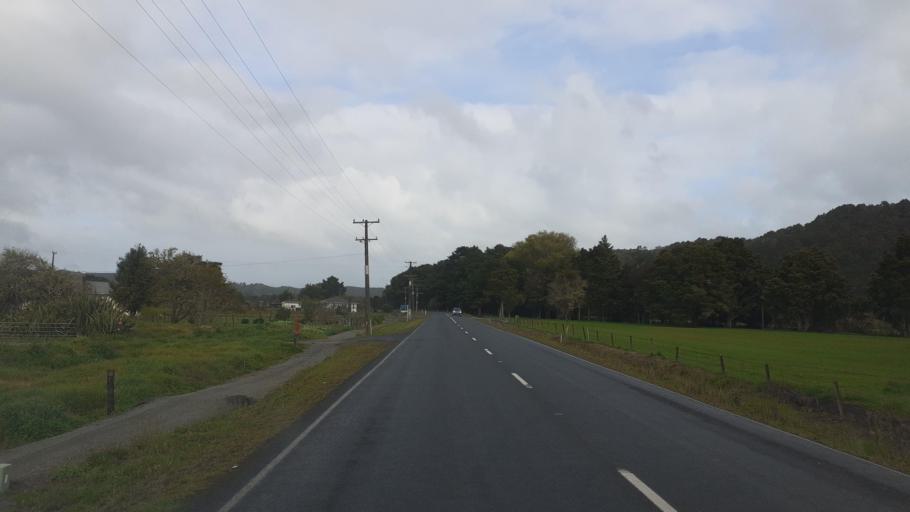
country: NZ
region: Northland
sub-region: Far North District
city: Moerewa
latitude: -35.3985
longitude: 173.9966
